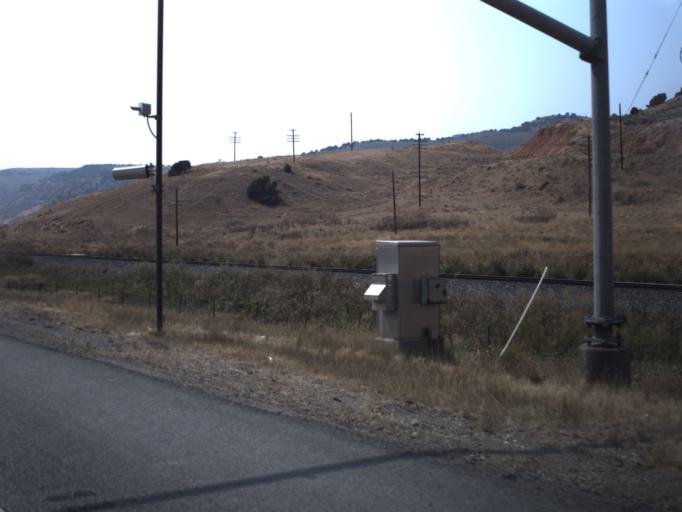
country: US
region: Utah
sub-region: Summit County
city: Coalville
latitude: 41.0879
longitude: -111.2303
